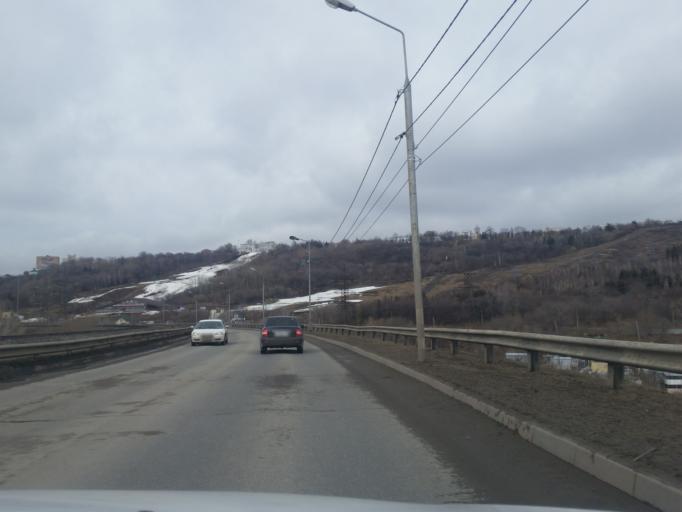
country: RU
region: Ulyanovsk
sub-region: Ulyanovskiy Rayon
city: Ulyanovsk
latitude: 54.3126
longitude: 48.4202
